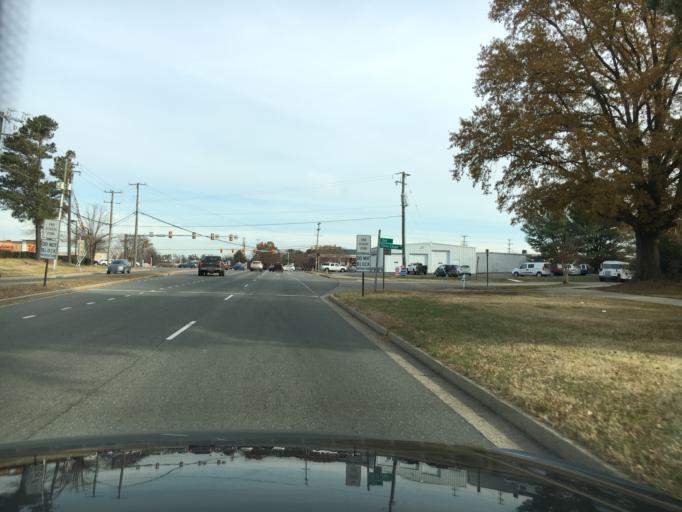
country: US
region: Virginia
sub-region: Henrico County
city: Short Pump
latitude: 37.6501
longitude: -77.6126
